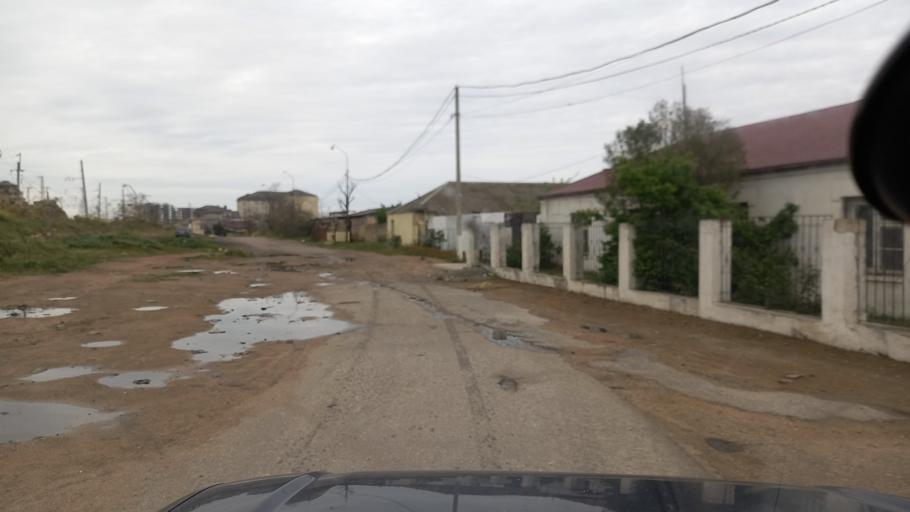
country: RU
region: Dagestan
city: Derbent
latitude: 42.0626
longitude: 48.3051
